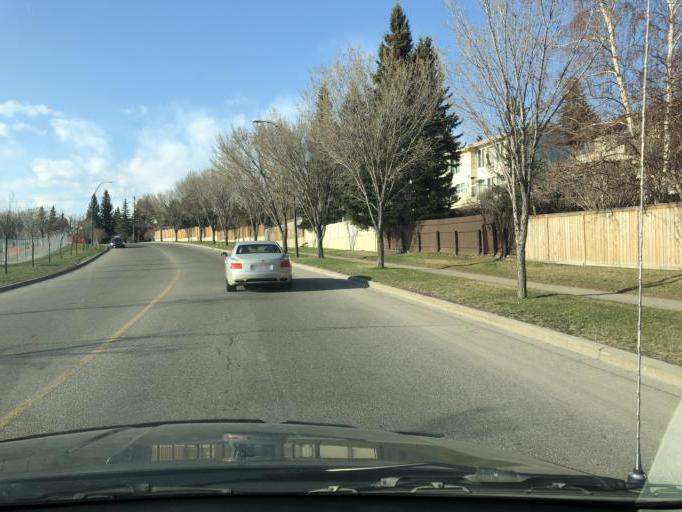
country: CA
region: Alberta
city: Calgary
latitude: 50.9637
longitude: -114.1020
